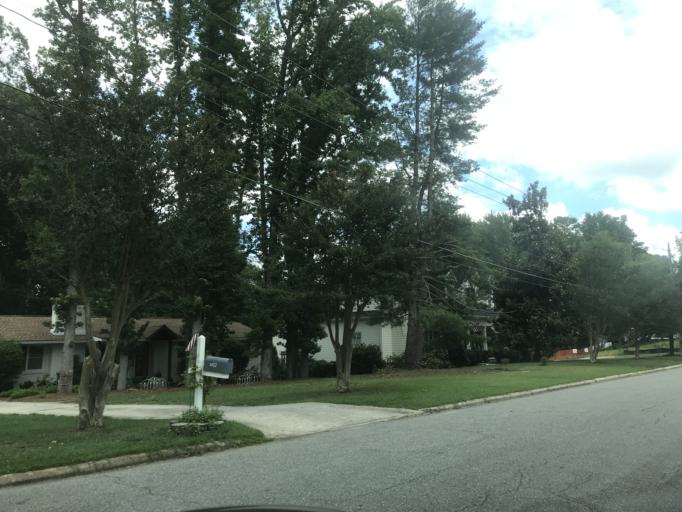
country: US
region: North Carolina
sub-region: Wake County
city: West Raleigh
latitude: 35.8412
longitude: -78.6356
